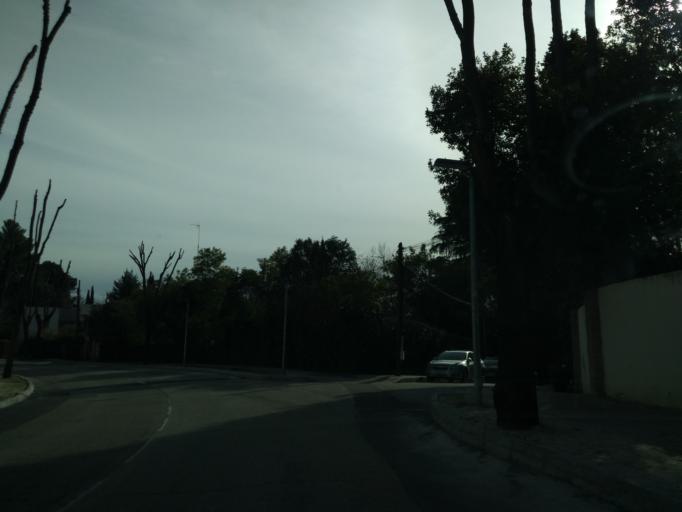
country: ES
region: Madrid
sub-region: Provincia de Madrid
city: Tetuan de las Victorias
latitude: 40.4626
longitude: -3.7294
